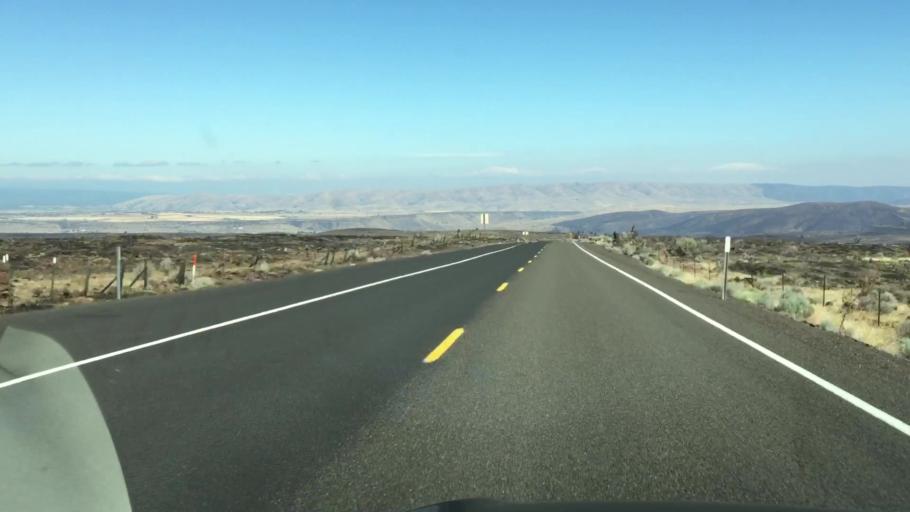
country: US
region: Oregon
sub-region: Jefferson County
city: Warm Springs
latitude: 45.1031
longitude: -121.0382
